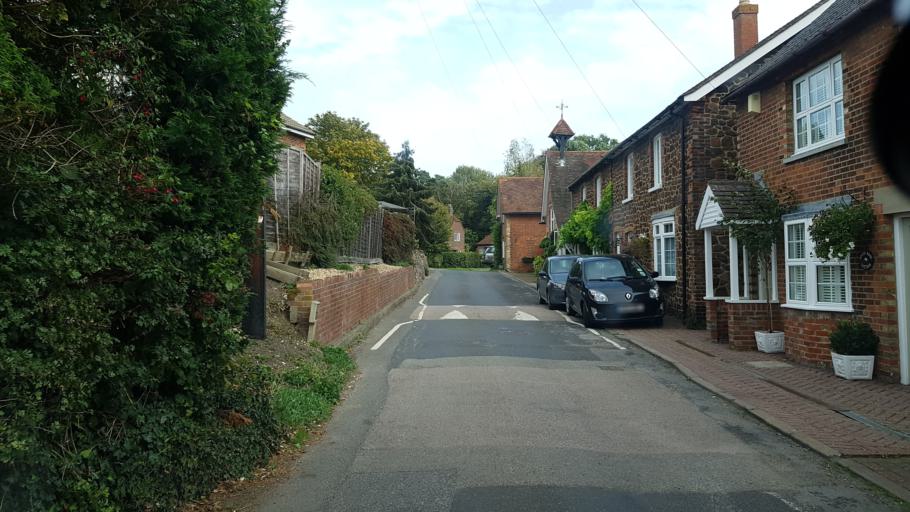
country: GB
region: England
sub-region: Kent
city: Meopham
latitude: 51.3169
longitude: 0.3552
